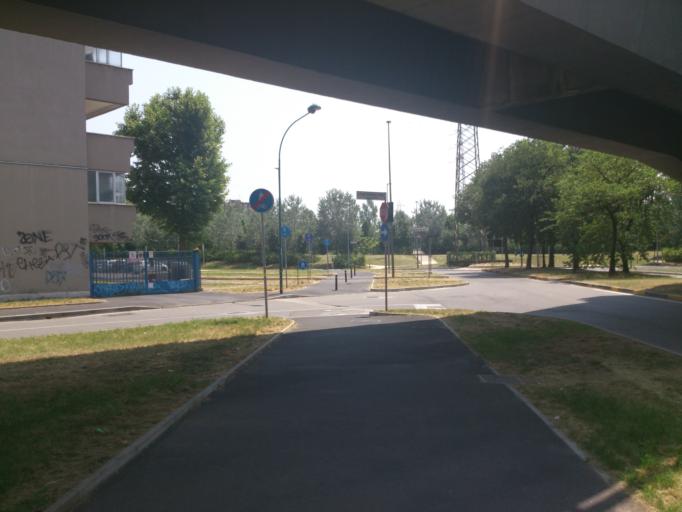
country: IT
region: Lombardy
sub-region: Citta metropolitana di Milano
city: Cologno Monzese
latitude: 45.5198
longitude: 9.2743
